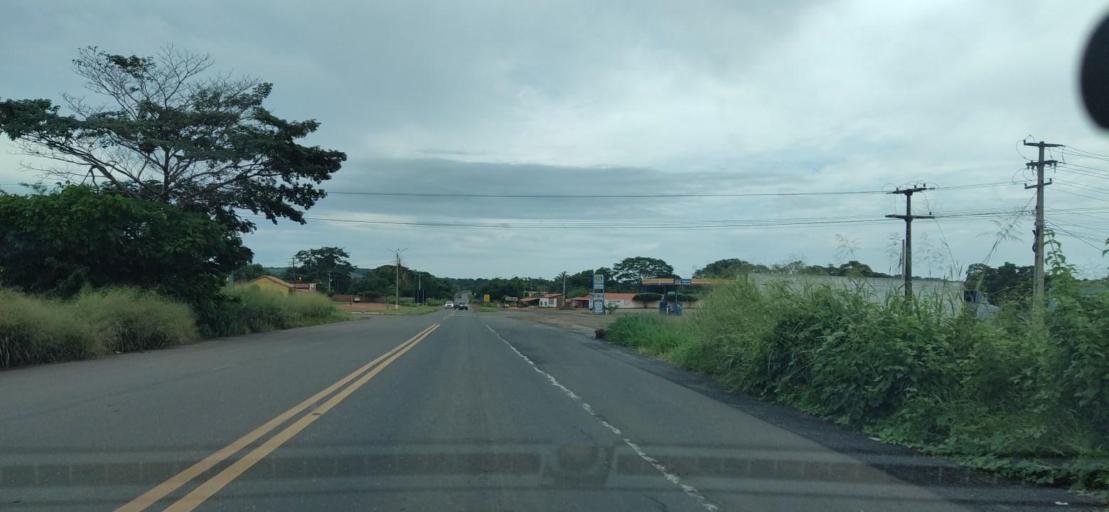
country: BR
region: Piaui
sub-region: Elesbao Veloso
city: Elesbao Veloso
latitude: -6.1895
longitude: -42.1200
